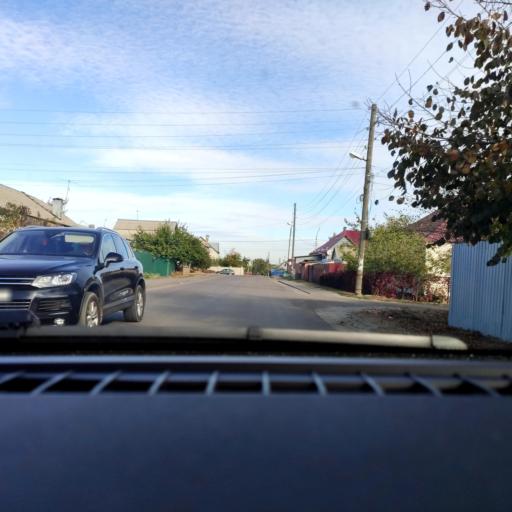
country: RU
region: Voronezj
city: Maslovka
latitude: 51.6093
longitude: 39.2207
